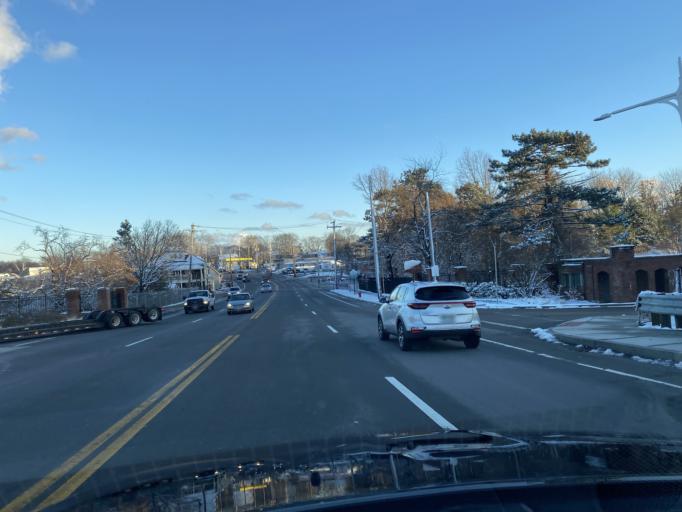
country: US
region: Massachusetts
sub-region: Norfolk County
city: Weymouth
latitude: 42.2435
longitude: -70.9632
